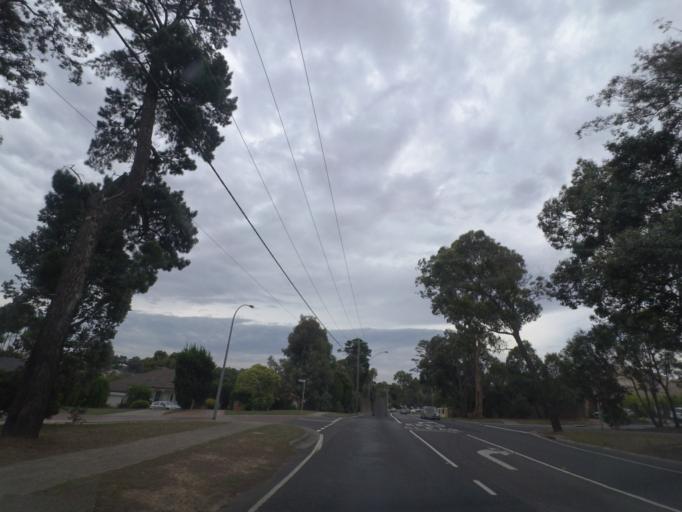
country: AU
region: Victoria
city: Saint Helena
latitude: -37.6816
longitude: 145.1306
